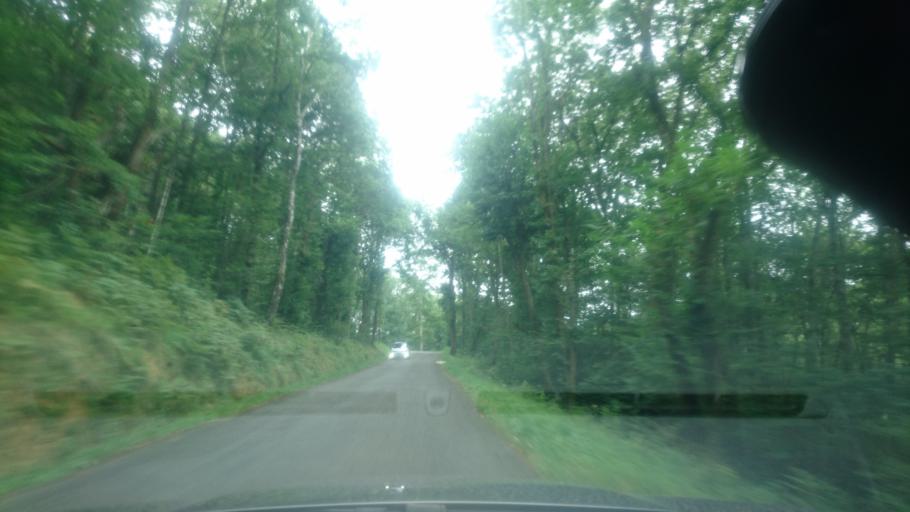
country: FR
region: Midi-Pyrenees
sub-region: Departement des Hautes-Pyrenees
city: Odos
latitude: 43.1415
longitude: 0.0505
